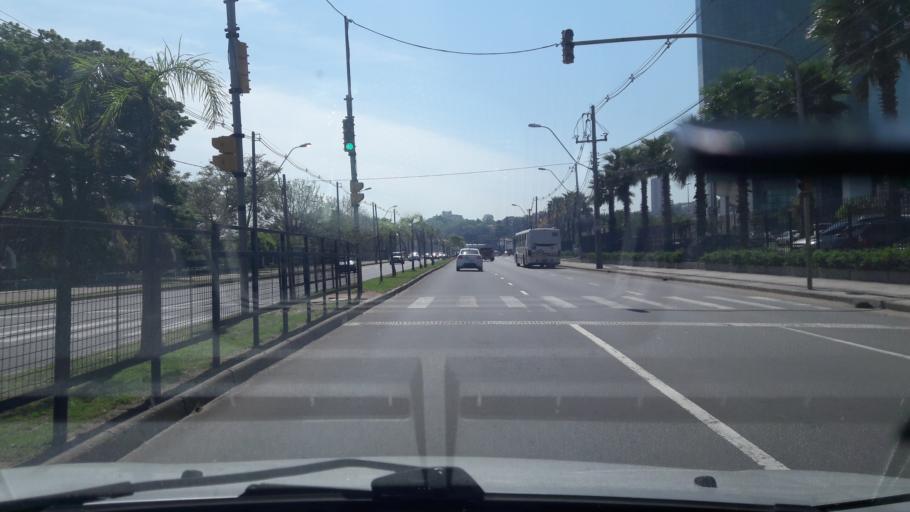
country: BR
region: Rio Grande do Sul
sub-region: Porto Alegre
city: Porto Alegre
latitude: -30.0854
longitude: -51.2475
